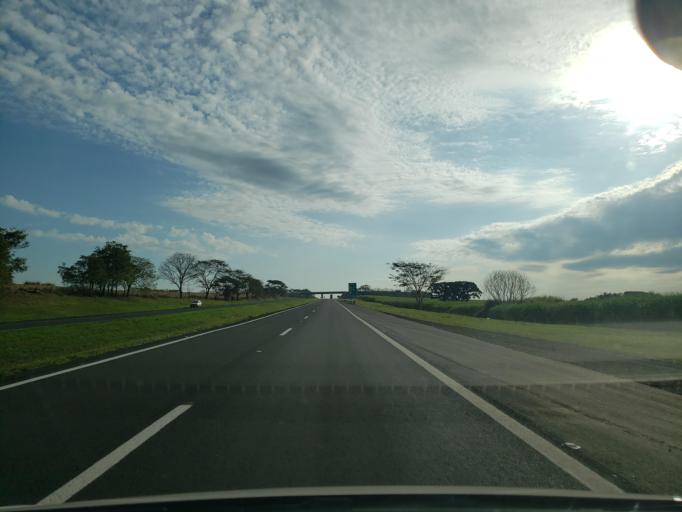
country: BR
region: Sao Paulo
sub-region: Valparaiso
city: Valparaiso
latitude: -21.2053
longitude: -50.7879
